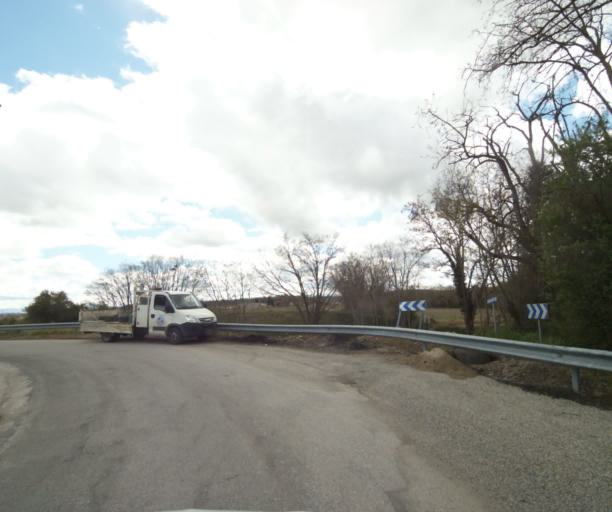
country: FR
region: Midi-Pyrenees
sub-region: Departement de l'Ariege
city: Saverdun
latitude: 43.2426
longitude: 1.5815
